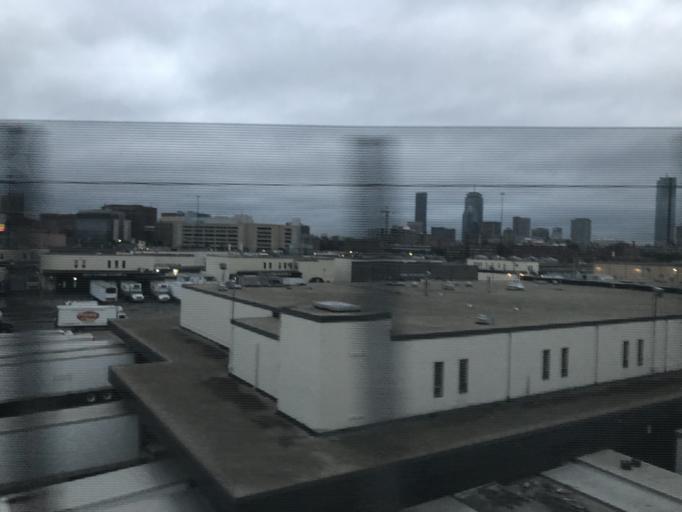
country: US
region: Massachusetts
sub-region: Suffolk County
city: South Boston
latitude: 42.3351
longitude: -71.0611
